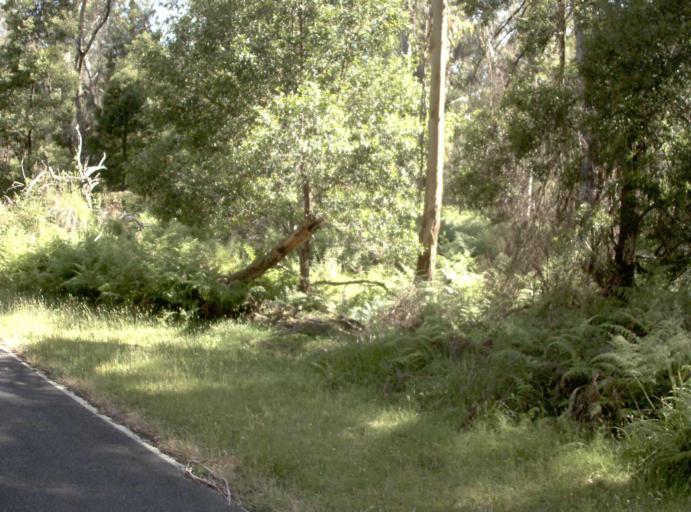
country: AU
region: New South Wales
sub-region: Bombala
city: Bombala
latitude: -37.3721
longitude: 148.6807
